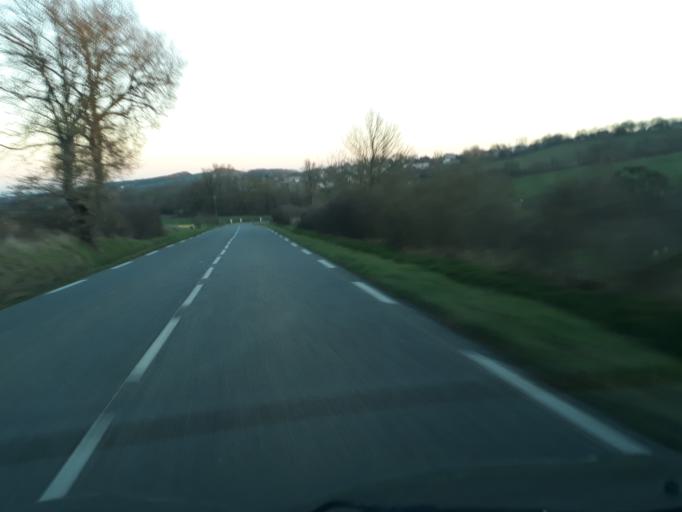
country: FR
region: Midi-Pyrenees
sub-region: Departement du Gers
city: Pujaudran
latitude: 43.5701
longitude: 1.1309
